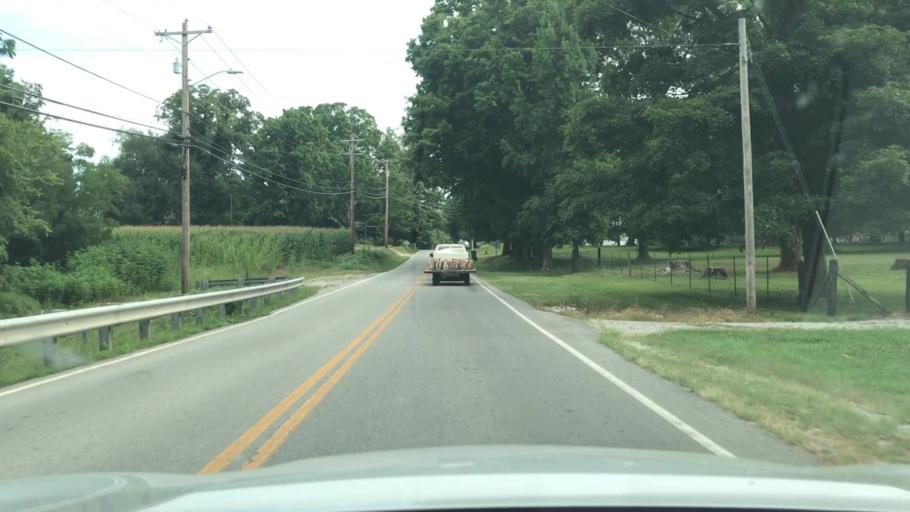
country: US
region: Kentucky
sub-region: Todd County
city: Elkton
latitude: 36.8139
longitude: -87.1529
